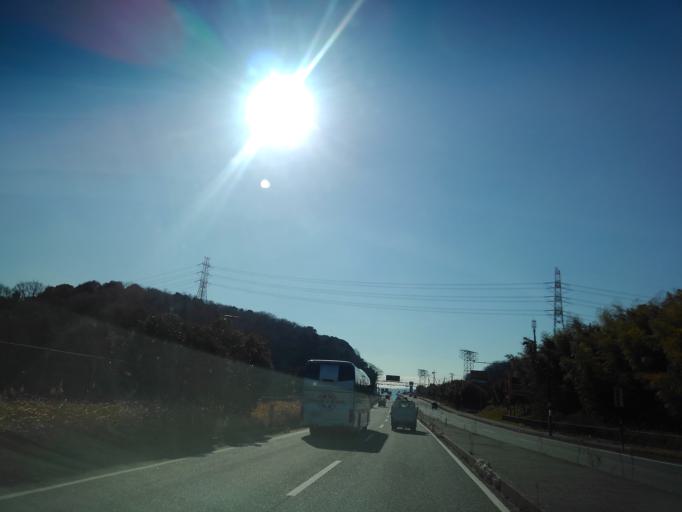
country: JP
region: Chiba
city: Kisarazu
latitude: 35.3424
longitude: 139.9208
